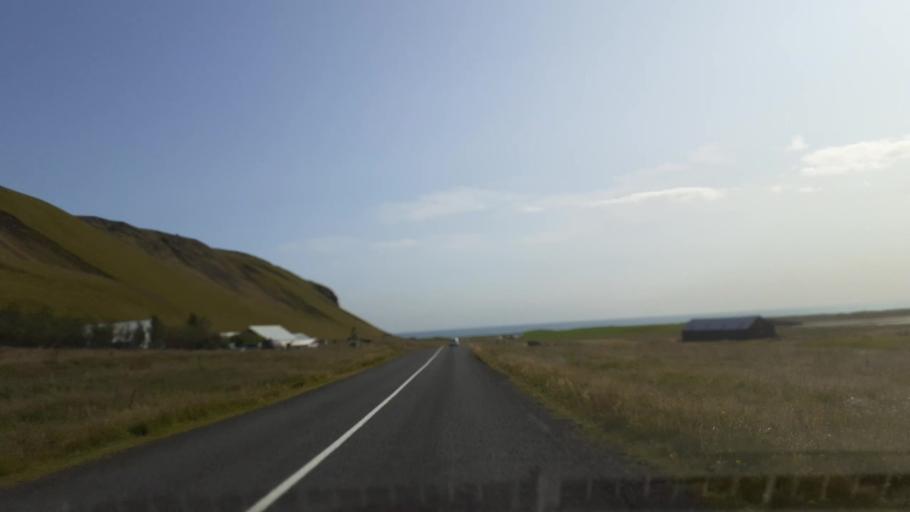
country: IS
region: South
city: Vestmannaeyjar
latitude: 63.4165
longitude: -19.0484
